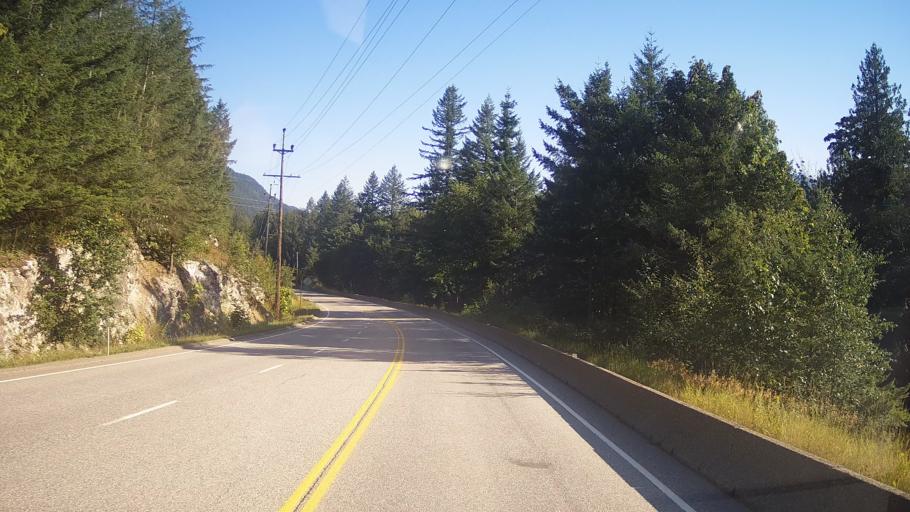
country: CA
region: British Columbia
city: Hope
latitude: 49.4282
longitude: -121.4378
